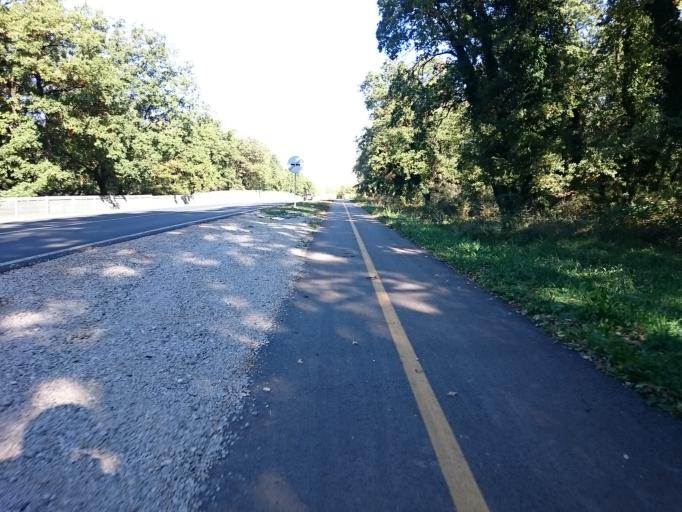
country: HR
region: Istarska
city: Umag
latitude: 45.4166
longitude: 13.5295
